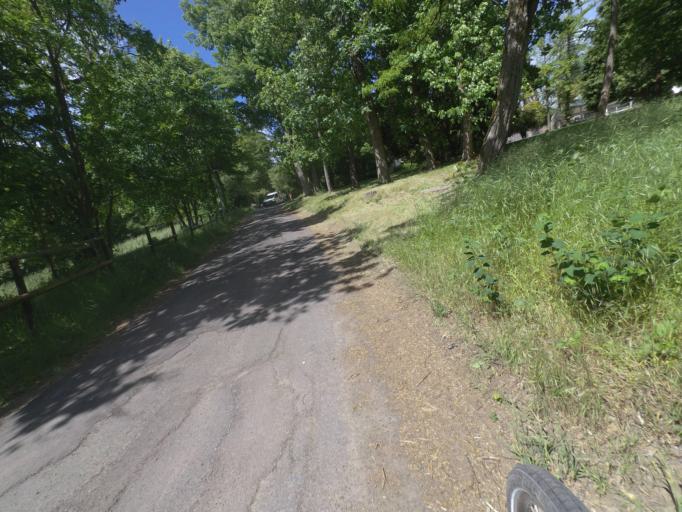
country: DE
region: Rheinland-Pfalz
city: Kirchheimbolanden
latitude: 49.6603
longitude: 8.0027
